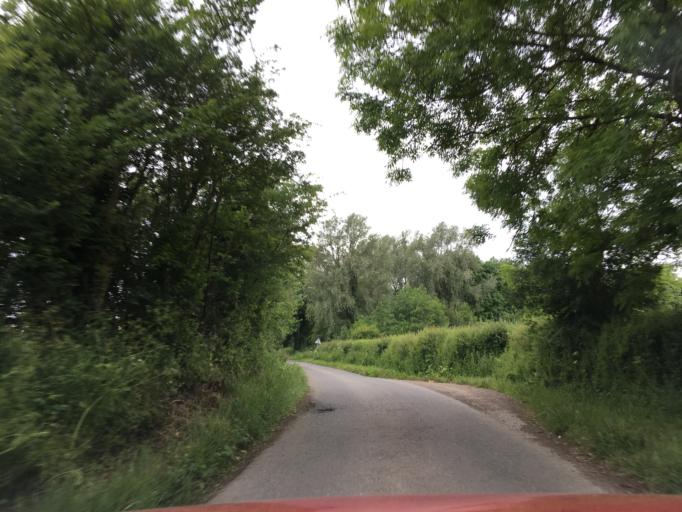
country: GB
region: England
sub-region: Gloucestershire
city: Tetbury
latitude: 51.6022
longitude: -2.1627
